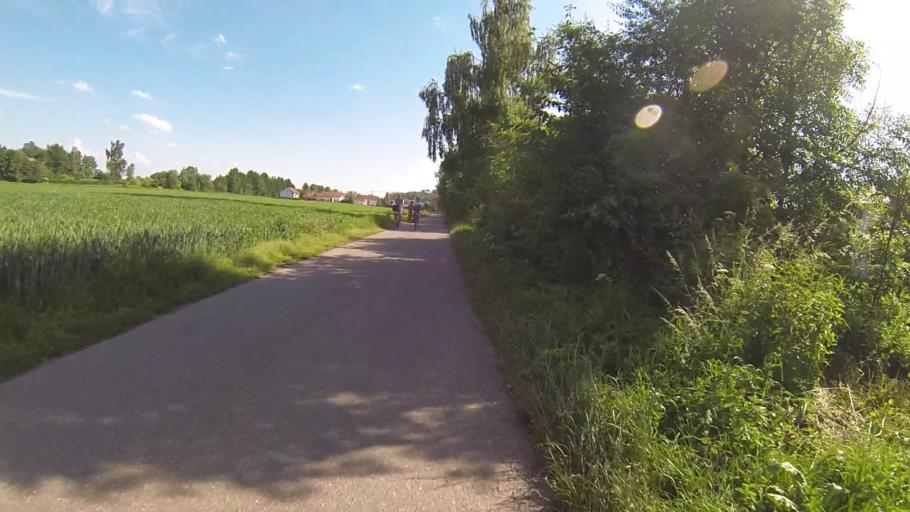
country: DE
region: Baden-Wuerttemberg
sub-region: Tuebingen Region
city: Laupheim
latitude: 48.1949
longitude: 9.8290
